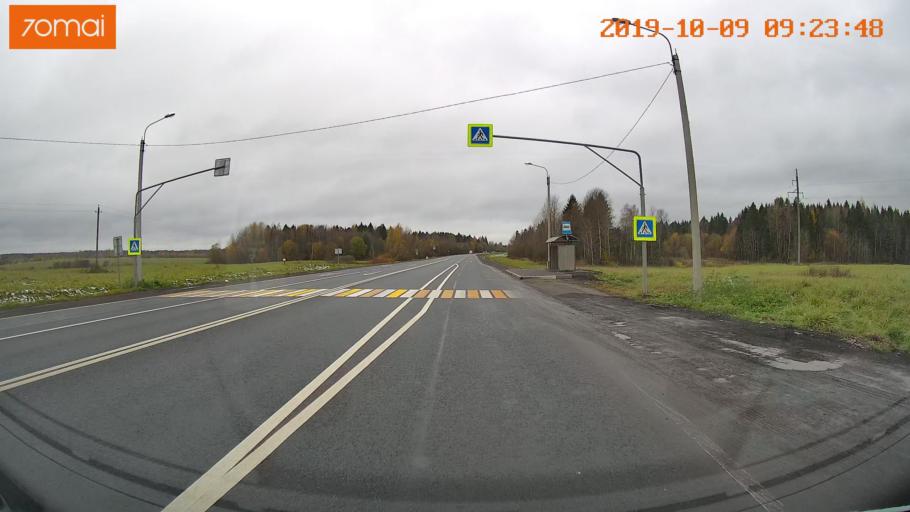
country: RU
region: Vologda
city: Vologda
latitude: 59.0733
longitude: 40.0258
